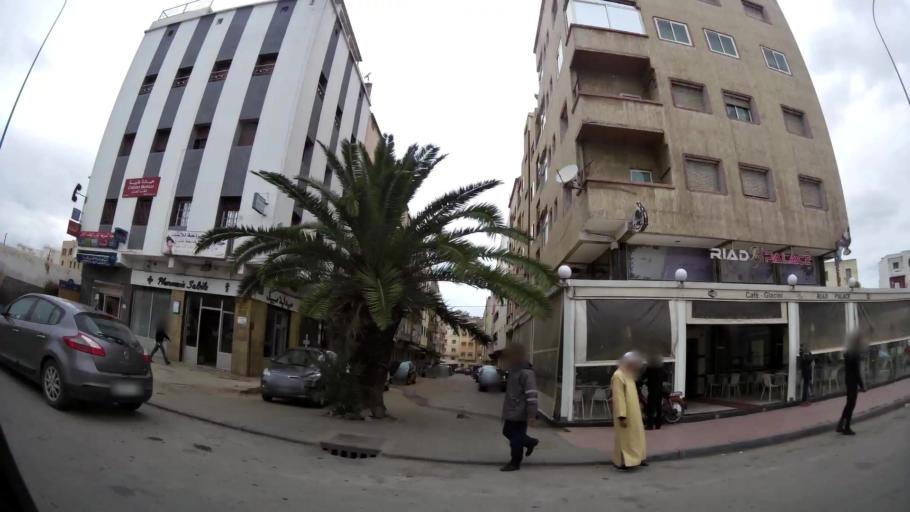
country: MA
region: Grand Casablanca
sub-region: Casablanca
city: Casablanca
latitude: 33.5688
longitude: -7.5599
